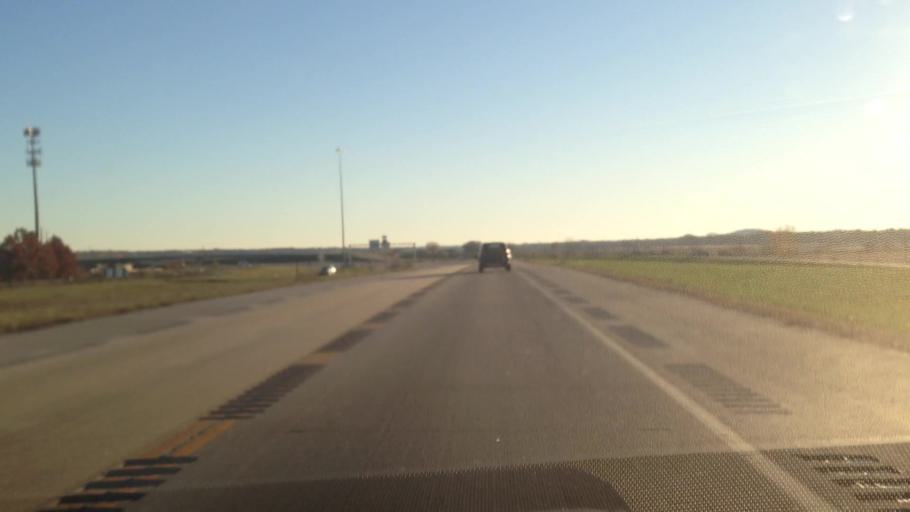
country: US
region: Kansas
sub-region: Douglas County
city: Lawrence
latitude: 38.9196
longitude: -95.2596
